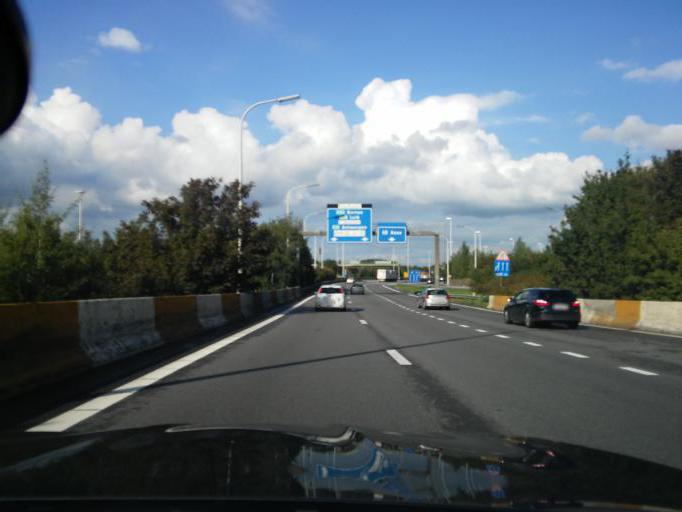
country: BE
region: Flanders
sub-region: Provincie Vlaams-Brabant
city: Dilbeek
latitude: 50.8762
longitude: 4.2770
